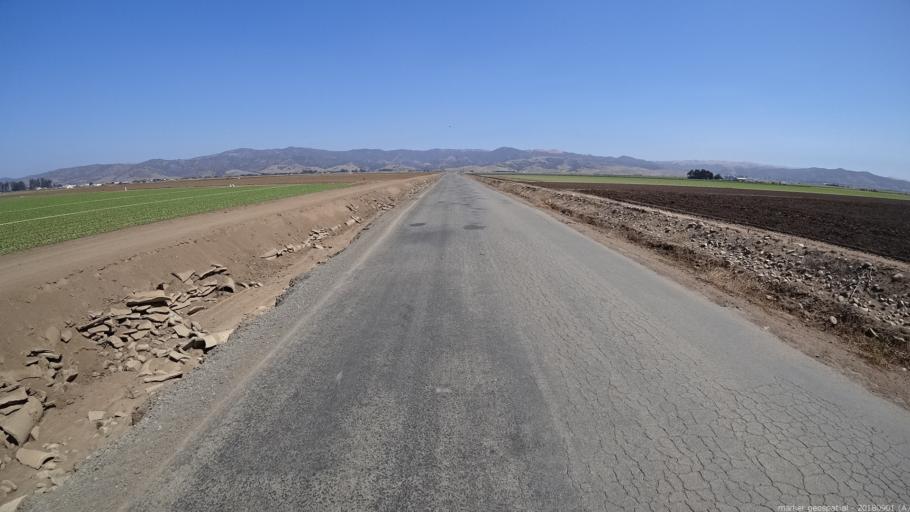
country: US
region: California
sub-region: Monterey County
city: Chualar
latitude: 36.5993
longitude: -121.5215
